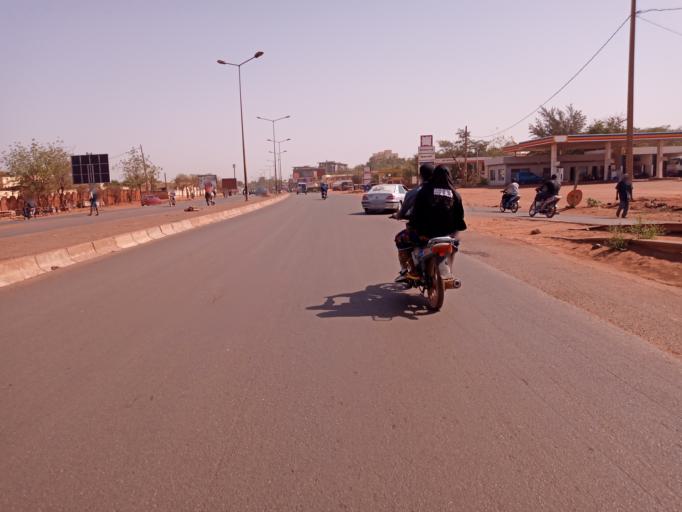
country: ML
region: Bamako
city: Bamako
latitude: 12.6099
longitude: -7.9957
